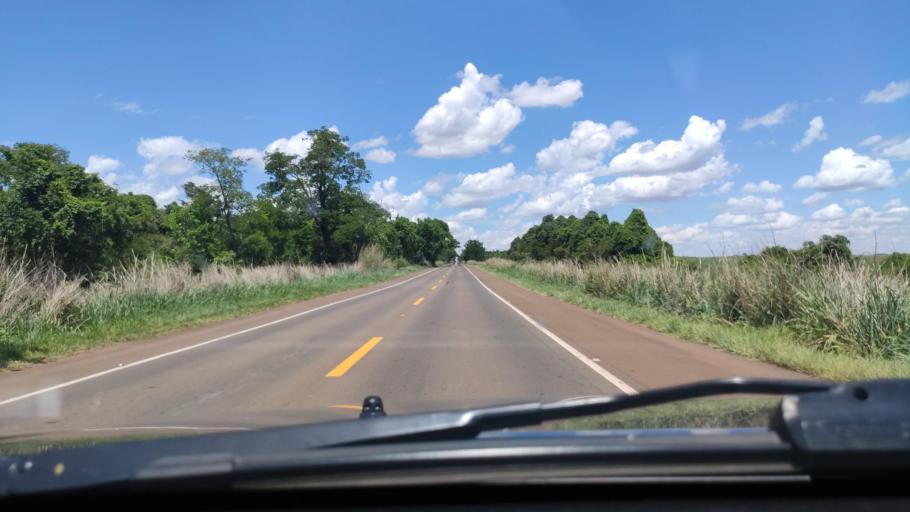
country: BR
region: Sao Paulo
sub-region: Boa Esperanca Do Sul
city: Boa Esperanca do Sul
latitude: -22.0692
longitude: -48.3832
